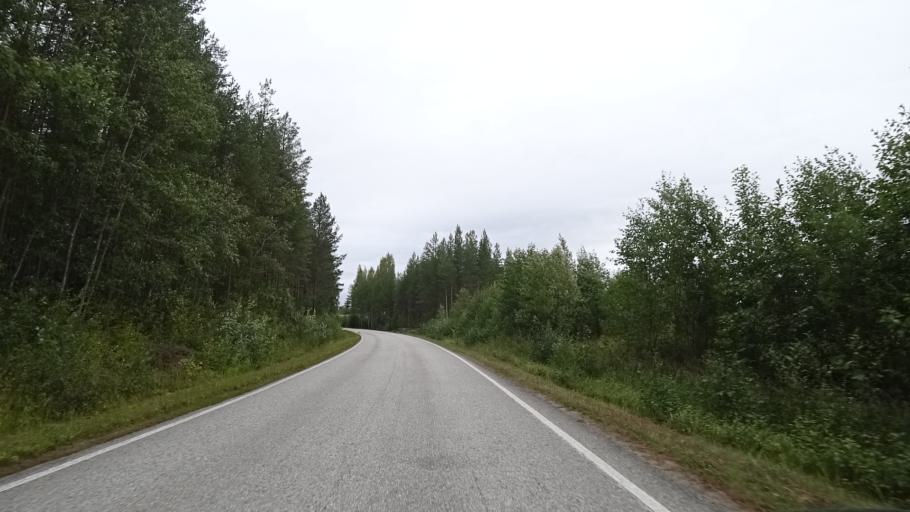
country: FI
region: North Karelia
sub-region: Pielisen Karjala
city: Lieksa
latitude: 63.3489
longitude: 30.2659
